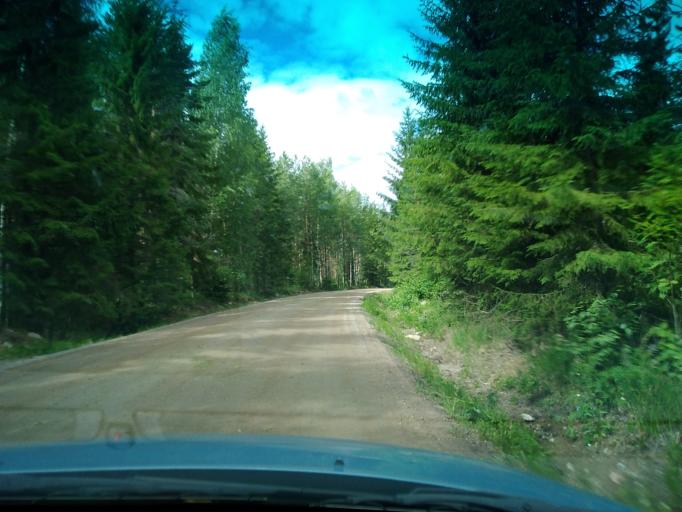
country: FI
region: Central Finland
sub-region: Saarijaervi-Viitasaari
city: Karstula
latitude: 62.7900
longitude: 24.9620
